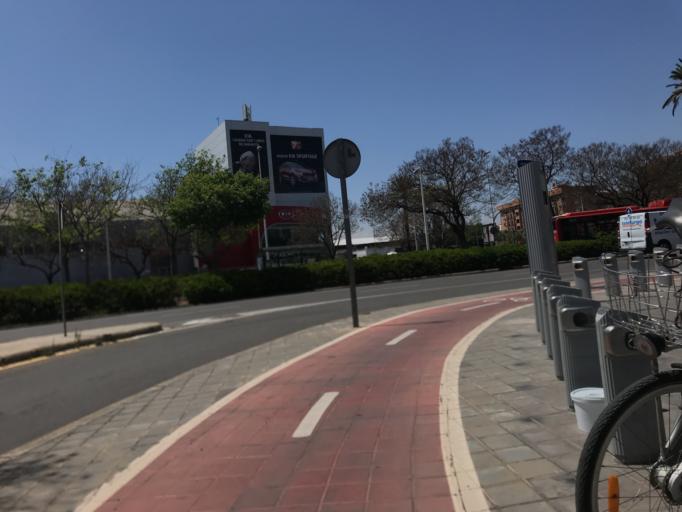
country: ES
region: Valencia
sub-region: Provincia de Valencia
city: Mislata
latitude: 39.4623
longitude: -0.4047
